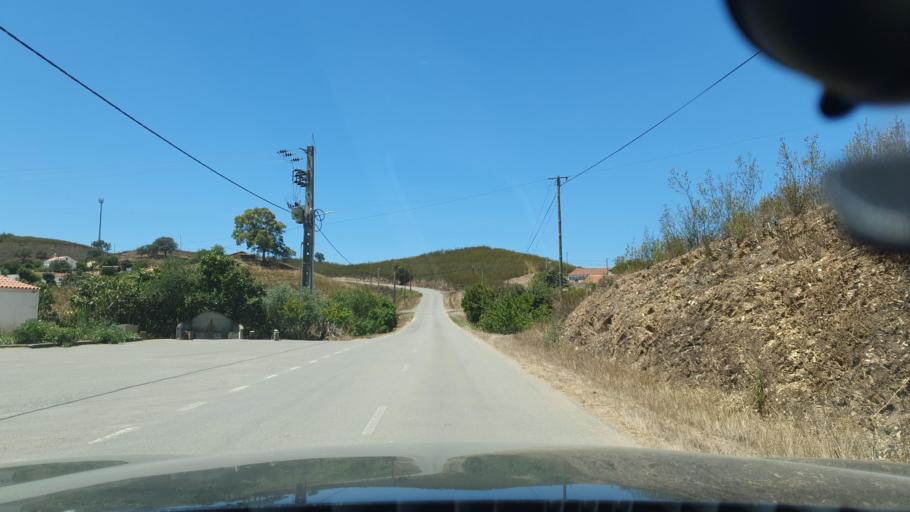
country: PT
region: Beja
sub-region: Ourique
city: Ourique
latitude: 37.5549
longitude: -8.4041
